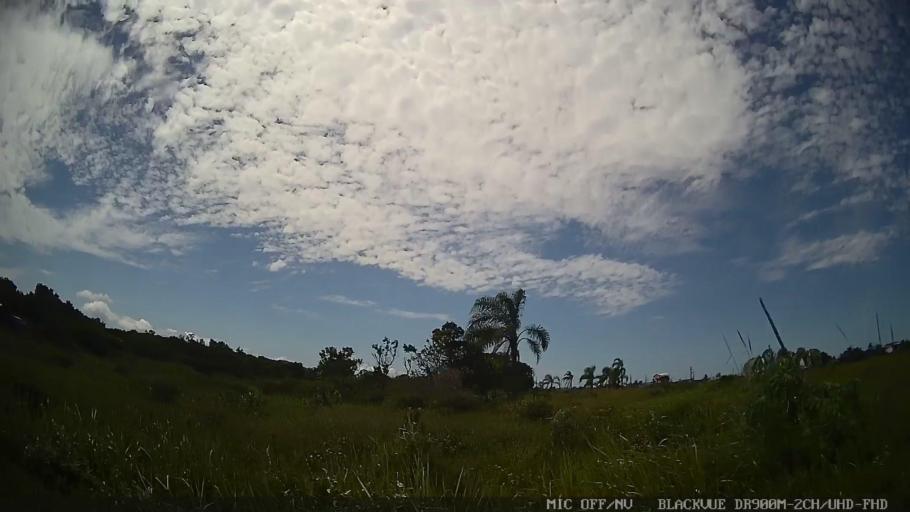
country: BR
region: Sao Paulo
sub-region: Iguape
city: Iguape
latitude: -24.7257
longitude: -47.5222
